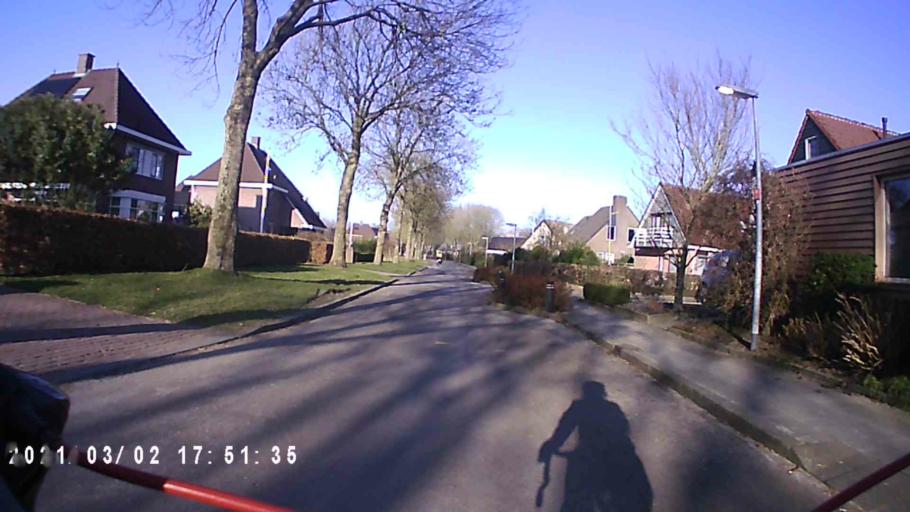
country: NL
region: Groningen
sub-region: Gemeente Zuidhorn
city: Aduard
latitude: 53.2556
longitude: 6.4547
